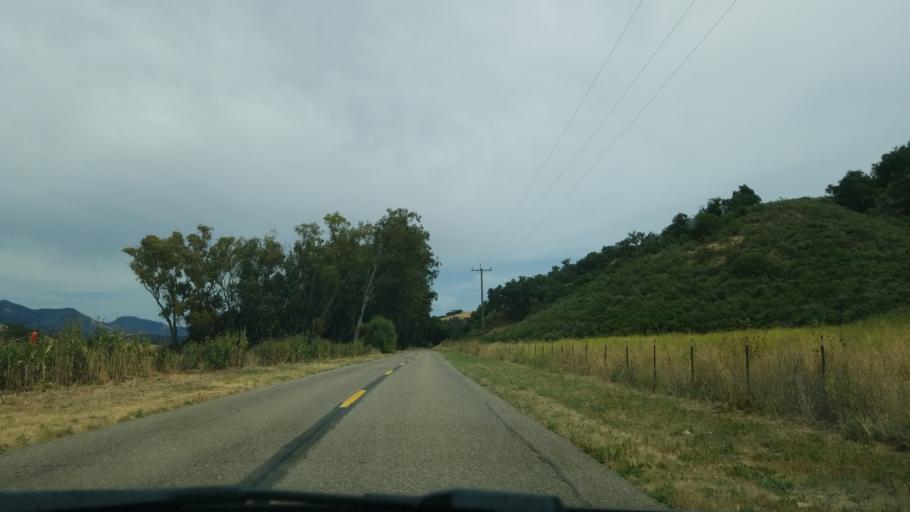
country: US
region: California
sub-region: Santa Barbara County
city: Los Alamos
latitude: 34.7813
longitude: -120.1614
